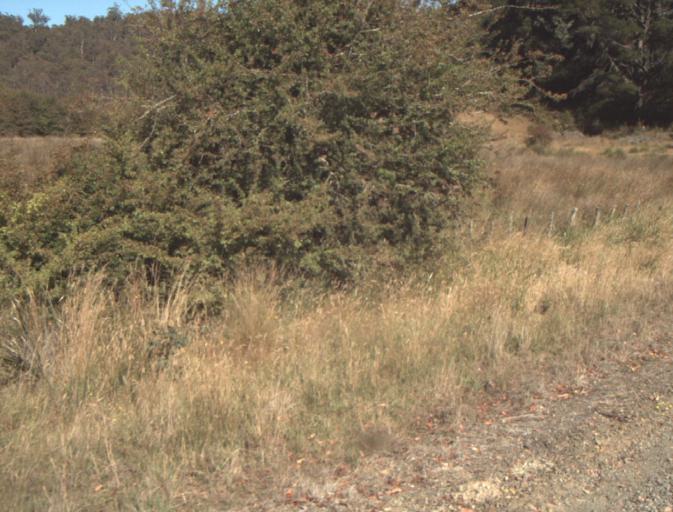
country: AU
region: Tasmania
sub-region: Launceston
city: Newstead
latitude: -41.3289
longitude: 147.3425
